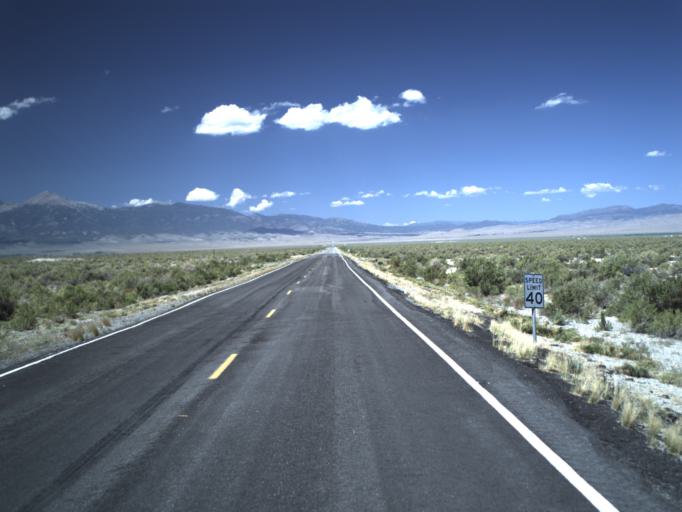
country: US
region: Nevada
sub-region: White Pine County
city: McGill
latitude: 39.0483
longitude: -113.9334
